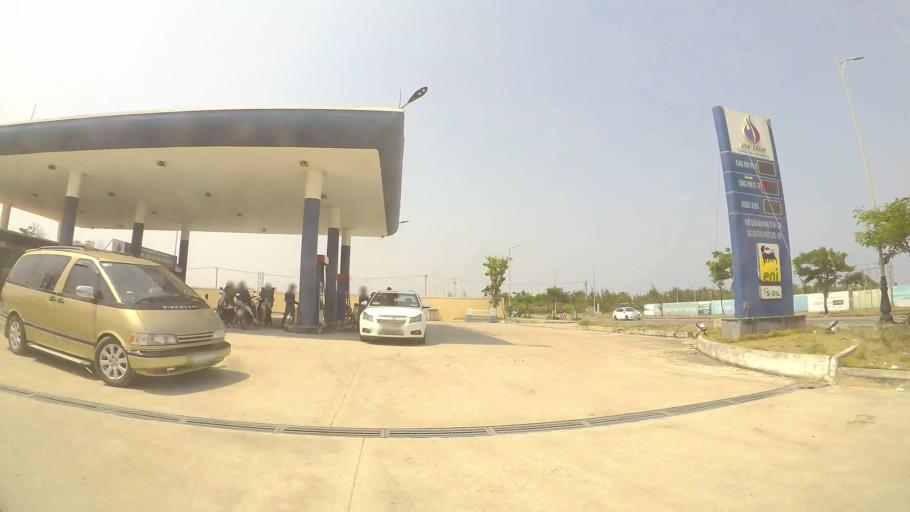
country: VN
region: Da Nang
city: Ngu Hanh Son
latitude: 15.9859
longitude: 108.2727
